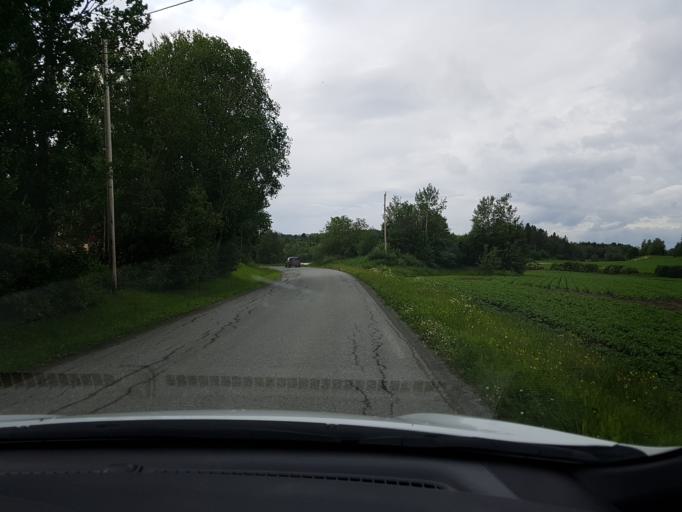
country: NO
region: Nord-Trondelag
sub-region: Frosta
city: Frosta
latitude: 63.6275
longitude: 10.7663
